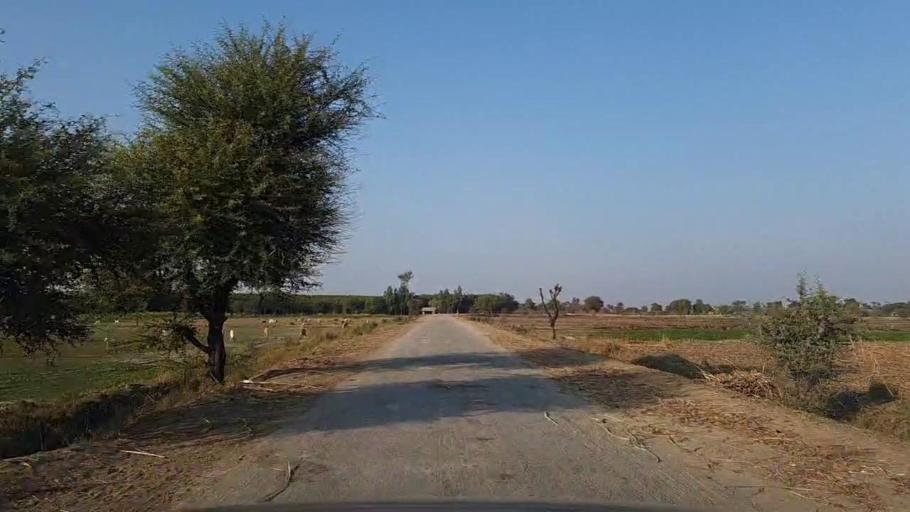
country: PK
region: Sindh
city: Tando Mittha Khan
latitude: 25.9388
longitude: 69.0713
